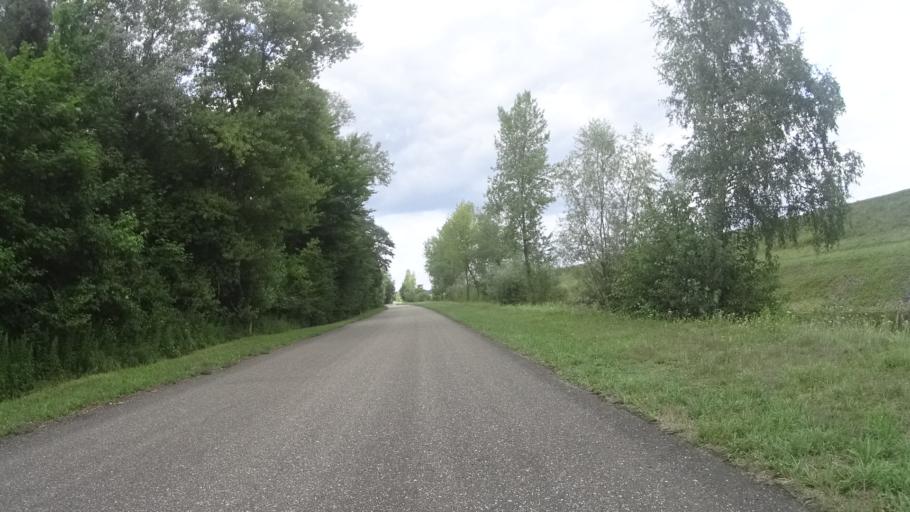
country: DE
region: Baden-Wuerttemberg
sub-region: Karlsruhe Region
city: Rheinmuenster
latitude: 48.7718
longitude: 8.0216
